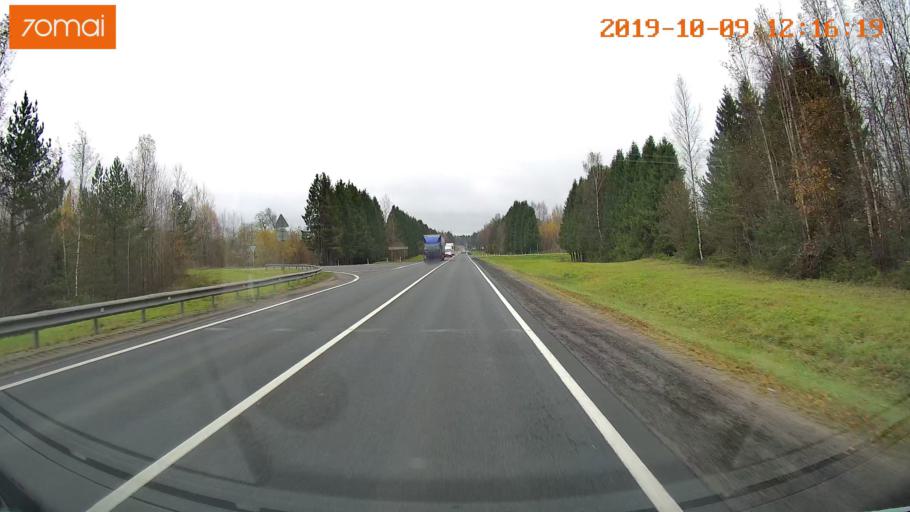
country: RU
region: Jaroslavl
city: Prechistoye
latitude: 58.4703
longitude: 40.3213
